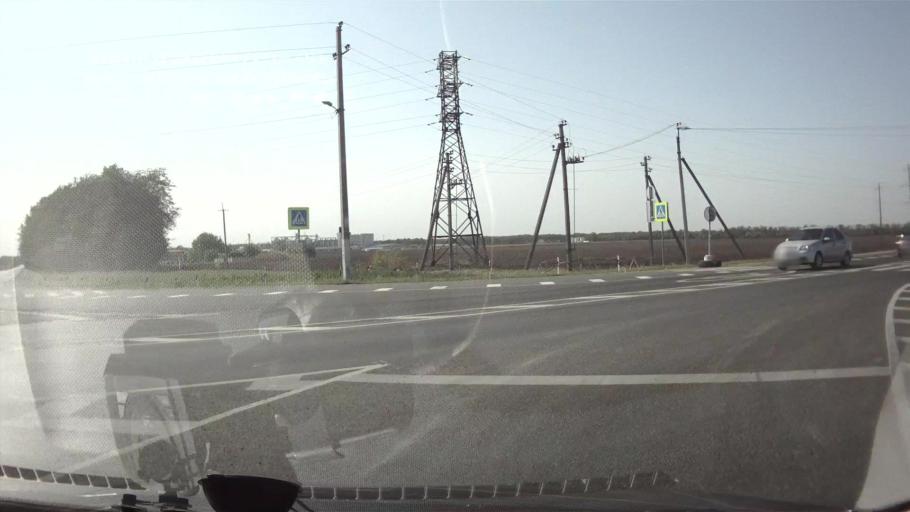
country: RU
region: Krasnodarskiy
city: Kavkazskaya
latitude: 45.4687
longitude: 40.6774
